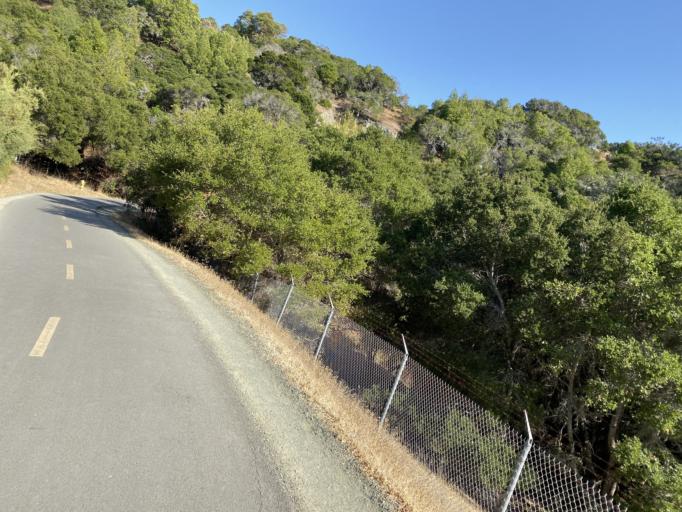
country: US
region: California
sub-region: San Mateo County
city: Highlands-Baywood Park
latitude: 37.5382
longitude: -122.3718
